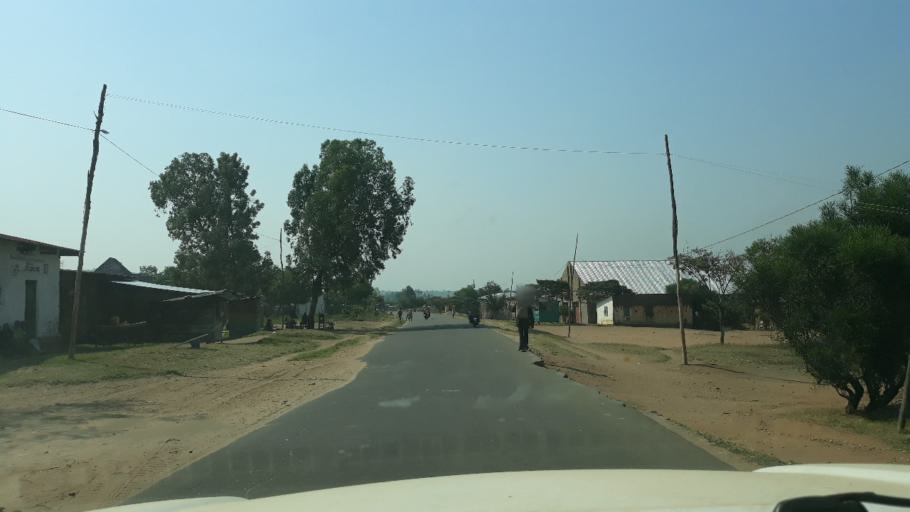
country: CD
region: South Kivu
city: Uvira
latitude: -3.2313
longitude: 29.1660
